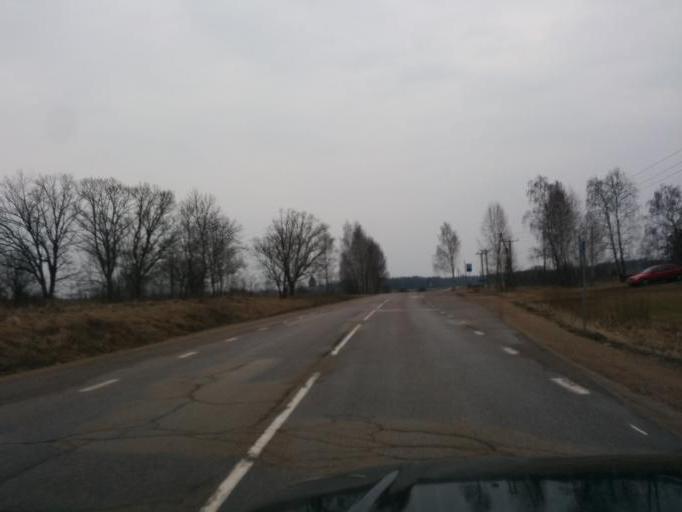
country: LV
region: Ikskile
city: Ikskile
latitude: 56.8205
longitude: 24.4466
